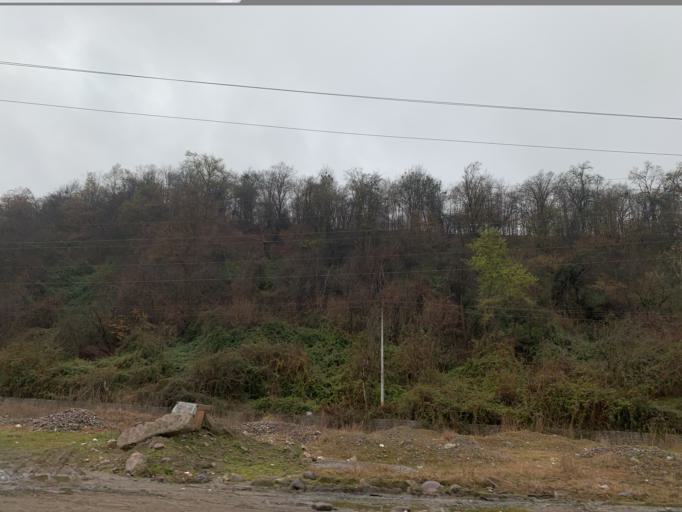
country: IR
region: Mazandaran
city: Amol
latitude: 36.3765
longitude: 52.3514
